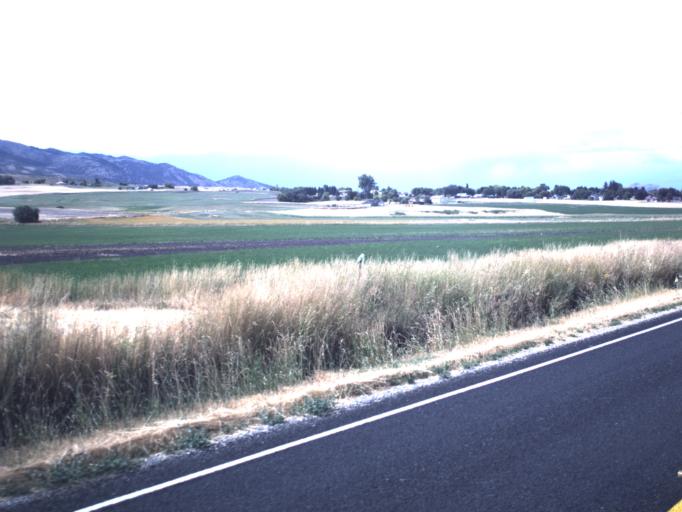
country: US
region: Utah
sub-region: Cache County
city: Benson
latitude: 41.9034
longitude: -112.0457
